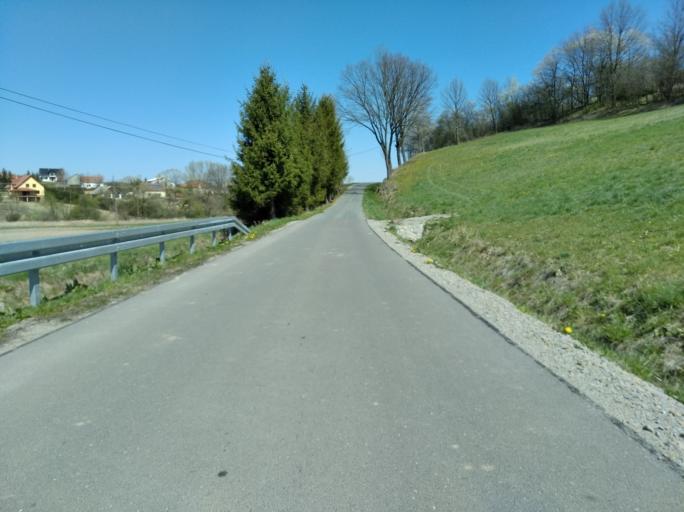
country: PL
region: Subcarpathian Voivodeship
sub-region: Powiat strzyzowski
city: Wisniowa
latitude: 49.9094
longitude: 21.6953
